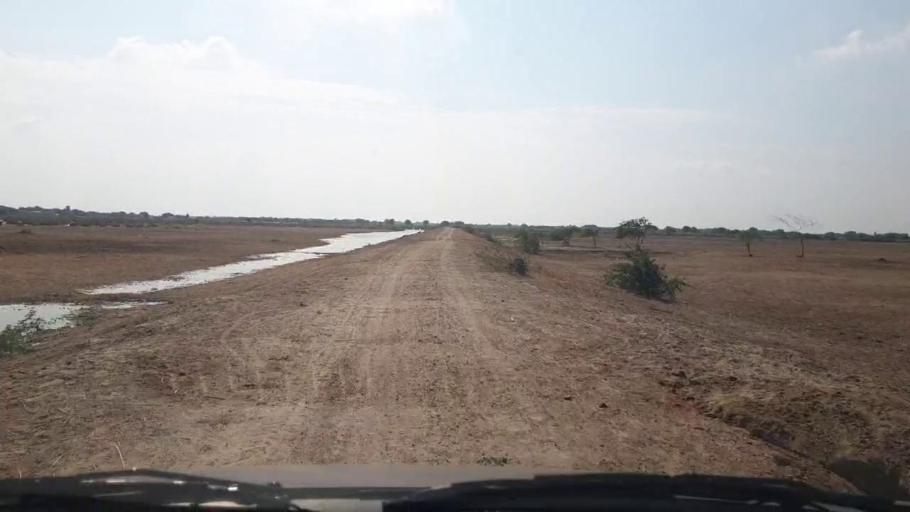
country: PK
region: Sindh
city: Badin
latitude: 24.4927
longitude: 68.6119
